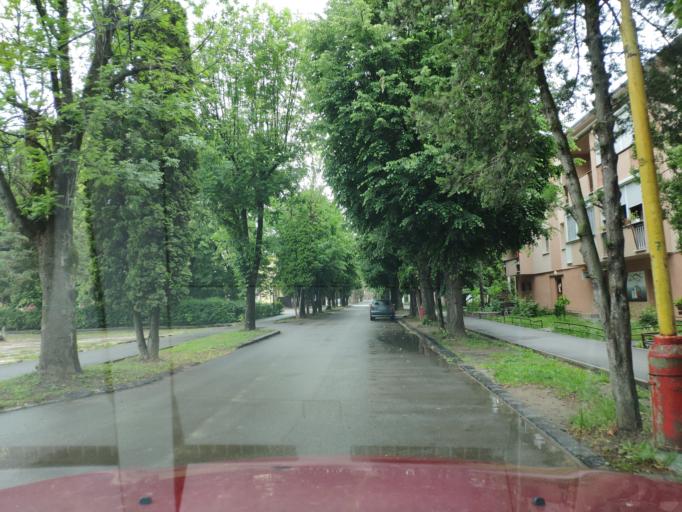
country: SK
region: Kosicky
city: Cierna nad Tisou
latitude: 48.4165
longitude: 22.0892
